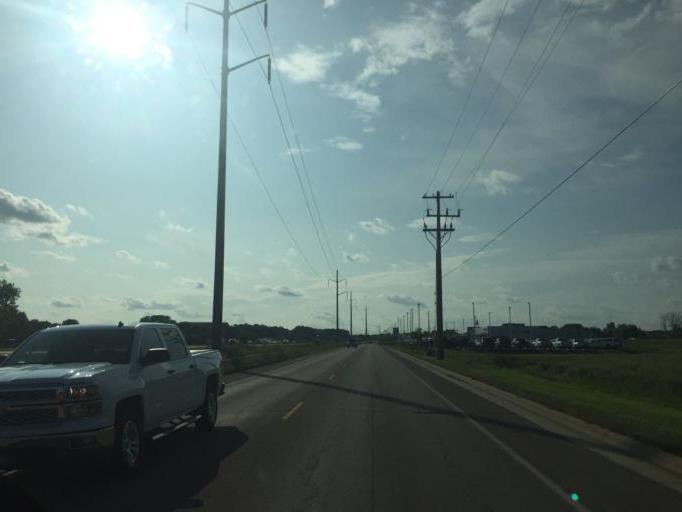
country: US
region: Minnesota
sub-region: Olmsted County
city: Rochester
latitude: 44.0354
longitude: -92.5088
